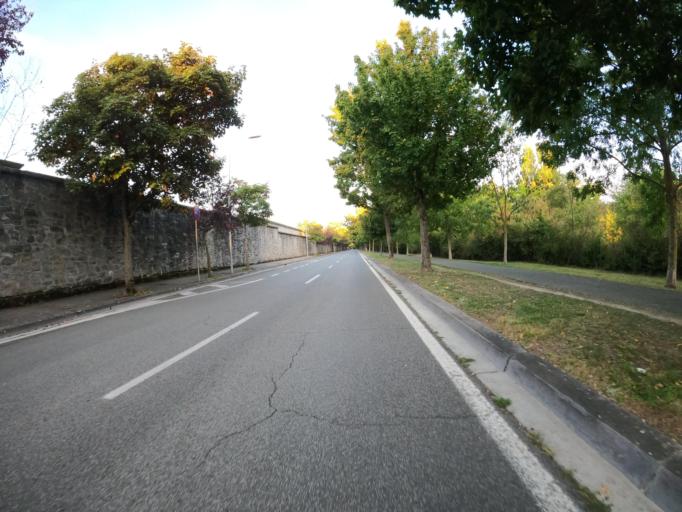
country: ES
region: Navarre
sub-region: Provincia de Navarra
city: Ermitagana
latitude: 42.8177
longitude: -1.6706
